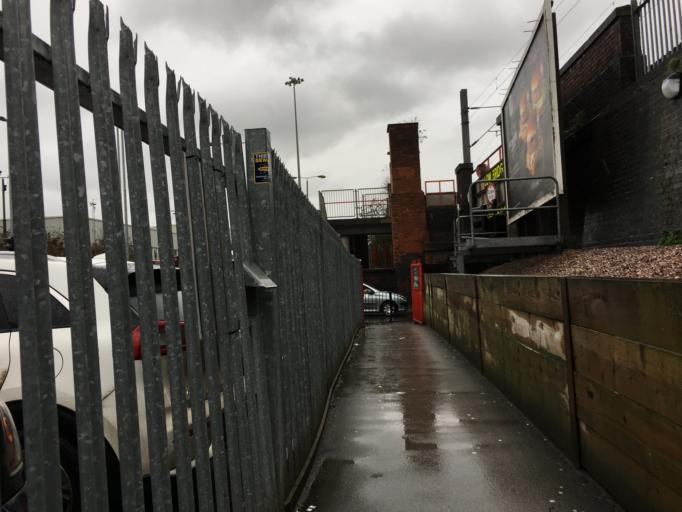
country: GB
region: England
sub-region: Warwickshire
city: Rugby
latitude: 52.3795
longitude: -1.2502
